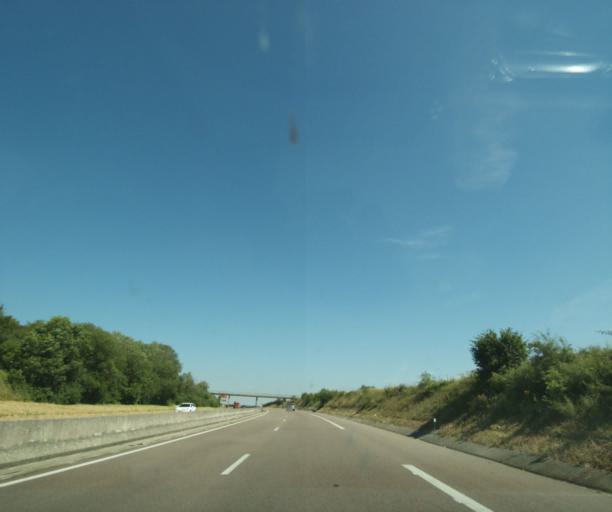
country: FR
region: Lorraine
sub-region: Departement des Vosges
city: Chatenois
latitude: 48.4011
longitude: 5.8806
